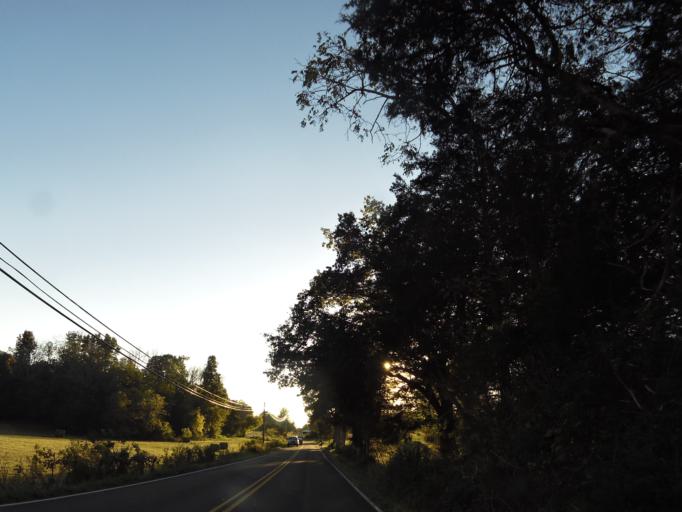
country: US
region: Tennessee
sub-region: Grainger County
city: Rutledge
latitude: 36.3097
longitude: -83.5546
